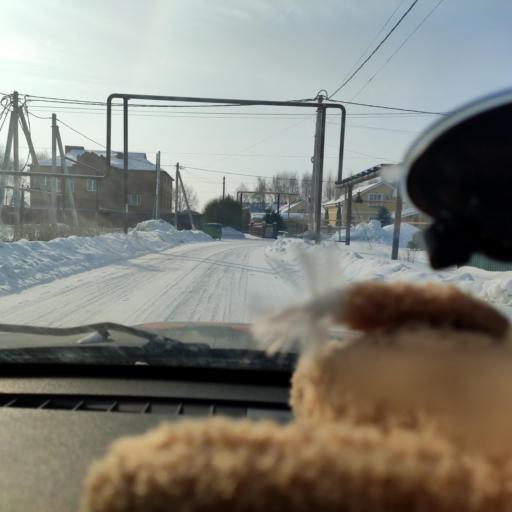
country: RU
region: Samara
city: Podstepki
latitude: 53.5111
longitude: 49.1198
